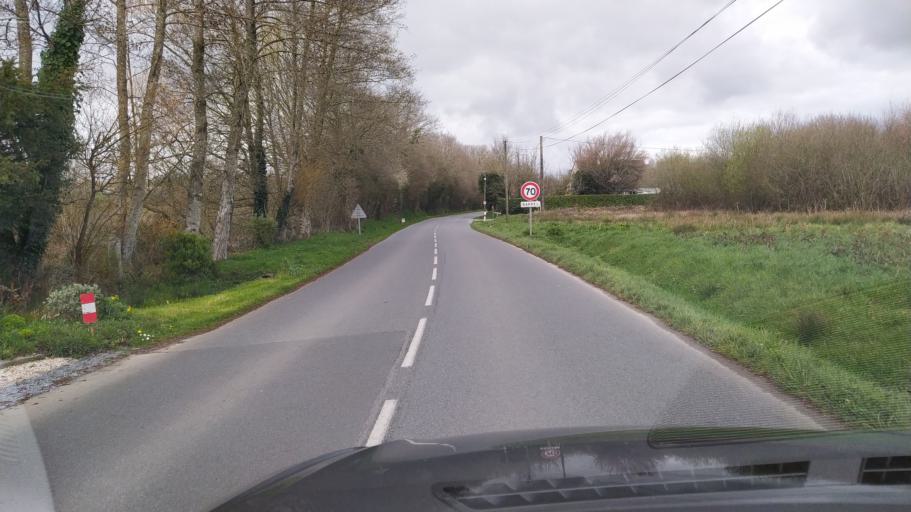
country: FR
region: Brittany
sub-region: Departement du Finistere
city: Bodilis
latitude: 48.5187
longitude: -4.1139
